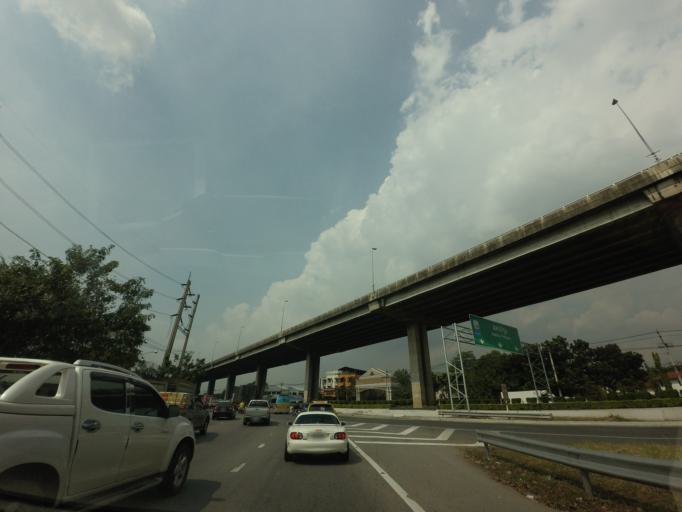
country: TH
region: Bangkok
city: Taling Chan
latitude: 13.7831
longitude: 100.4054
